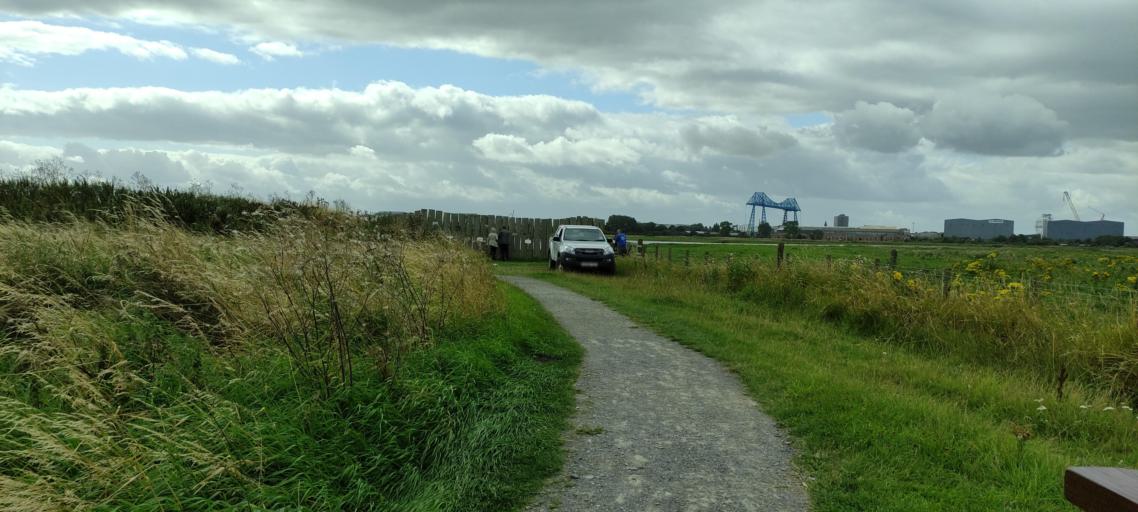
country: GB
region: England
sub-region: Middlesbrough
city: Middlesbrough
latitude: 54.5960
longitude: -1.2221
